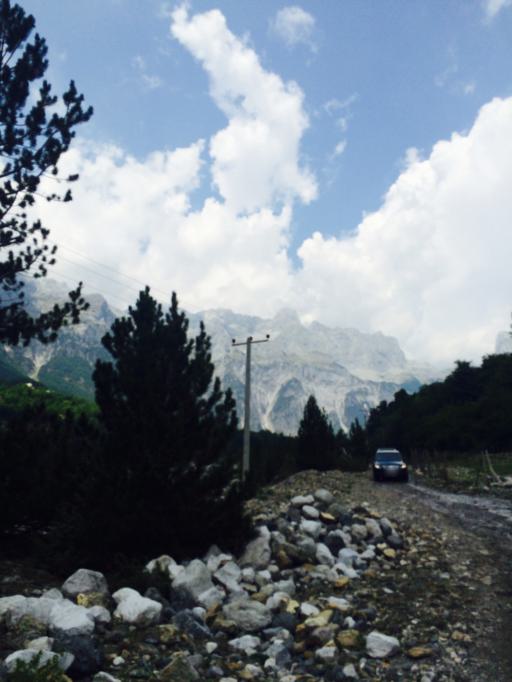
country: AL
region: Shkoder
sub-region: Rrethi i Shkodres
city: Nicaj-Shale
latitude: 42.3963
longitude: 19.7730
